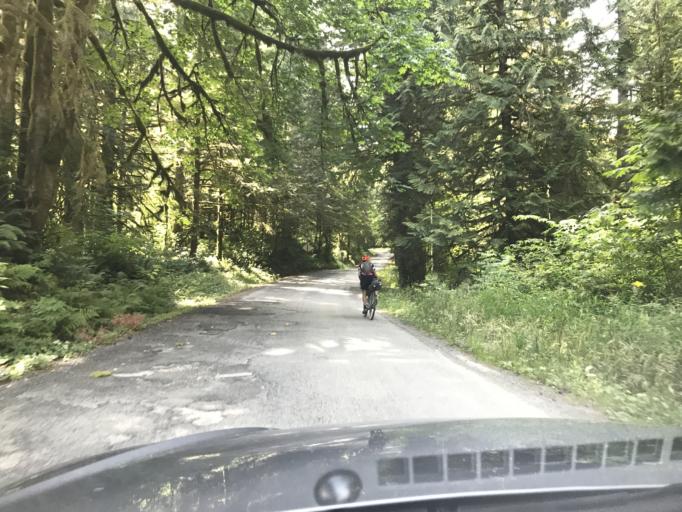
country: US
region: Washington
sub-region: King County
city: Hobart
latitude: 47.4148
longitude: -121.9261
